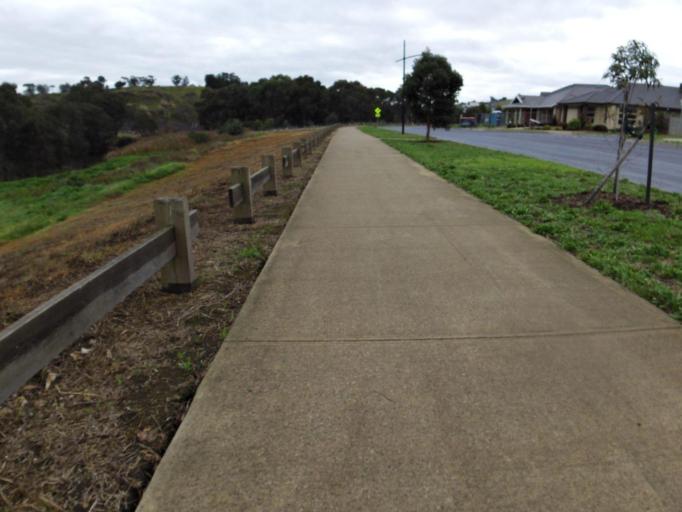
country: AU
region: Victoria
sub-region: Greater Geelong
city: Hamlyn Heights
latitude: -38.1392
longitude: 144.3100
